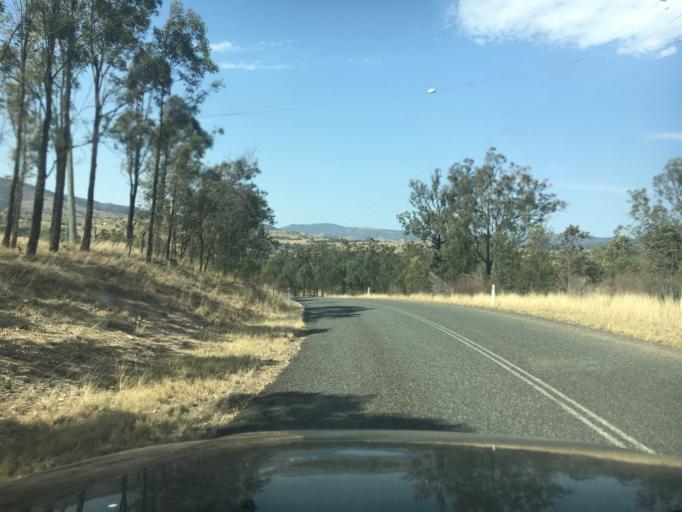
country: AU
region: New South Wales
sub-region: Singleton
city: Singleton
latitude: -32.5096
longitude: 151.3036
